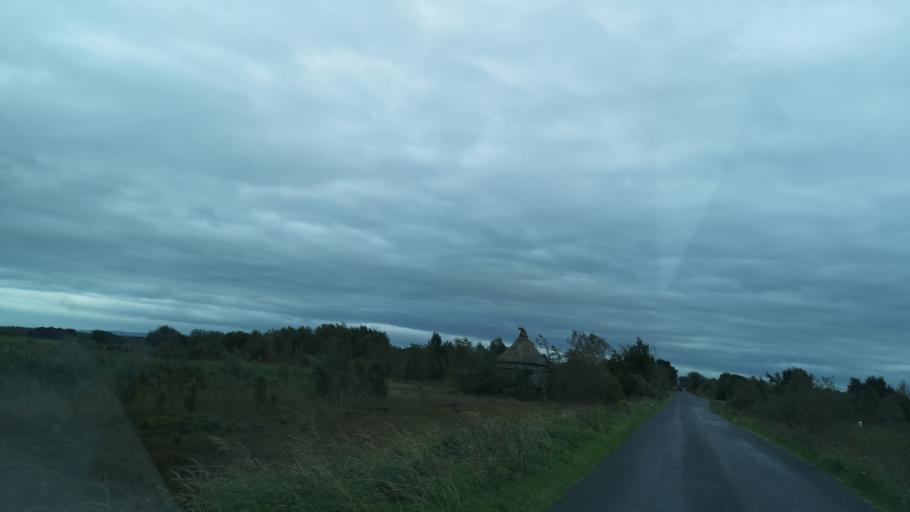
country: IE
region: Leinster
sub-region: Uibh Fhaili
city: Ferbane
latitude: 53.2178
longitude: -7.7260
